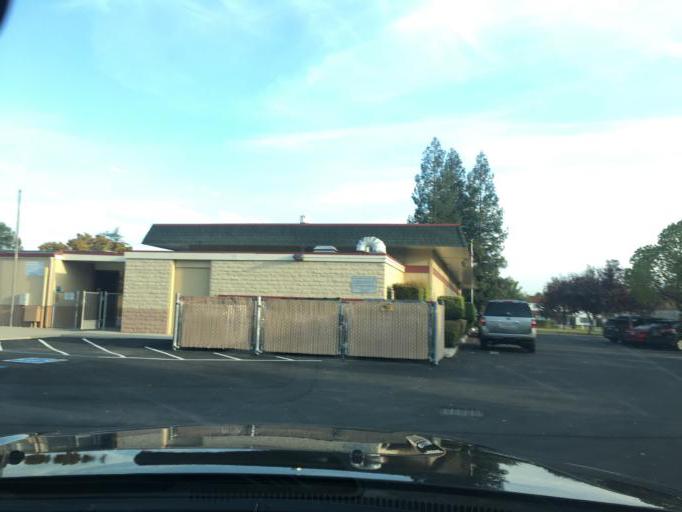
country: US
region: California
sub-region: Santa Clara County
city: Cambrian Park
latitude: 37.2197
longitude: -121.8692
